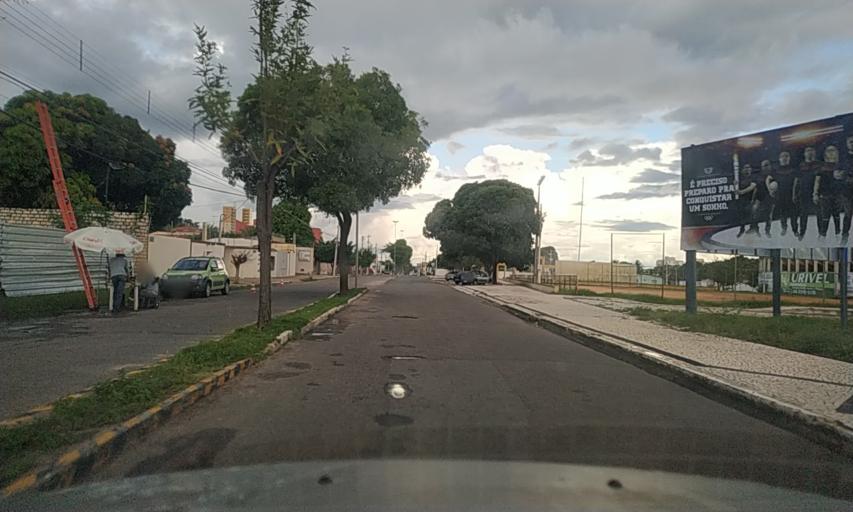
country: BR
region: Rio Grande do Norte
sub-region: Mossoro
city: Mossoro
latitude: -5.1842
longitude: -37.3569
